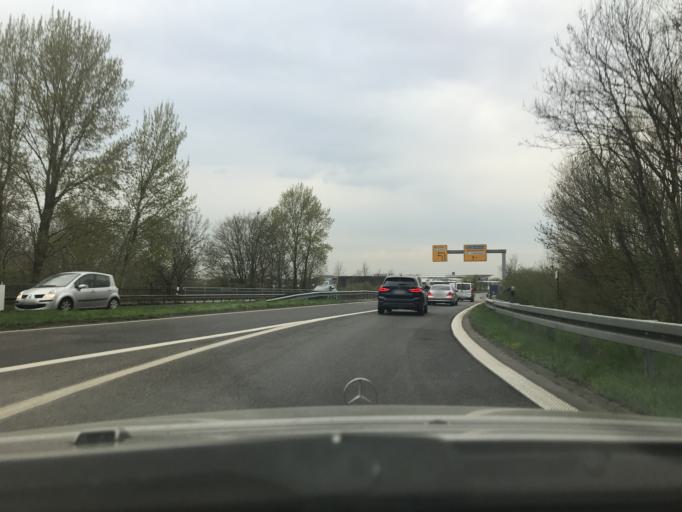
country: DE
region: North Rhine-Westphalia
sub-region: Regierungsbezirk Dusseldorf
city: Korschenbroich
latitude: 51.2222
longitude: 6.4907
